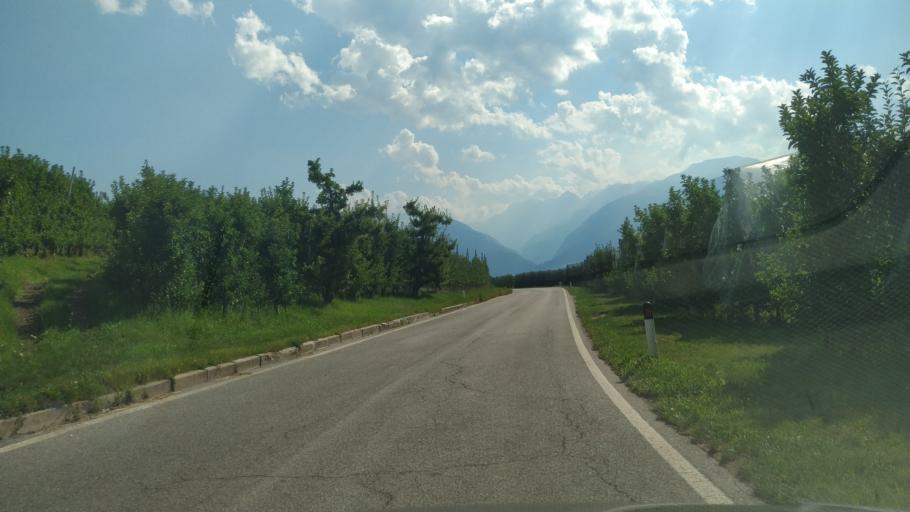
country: IT
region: Trentino-Alto Adige
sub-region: Provincia di Trento
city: Sanzeno
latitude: 46.3823
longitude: 11.0792
